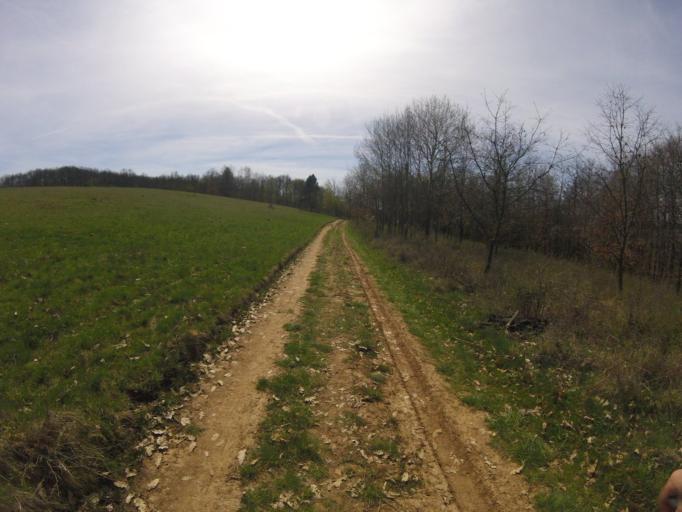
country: HU
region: Borsod-Abauj-Zemplen
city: Szendro
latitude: 48.4280
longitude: 20.7541
